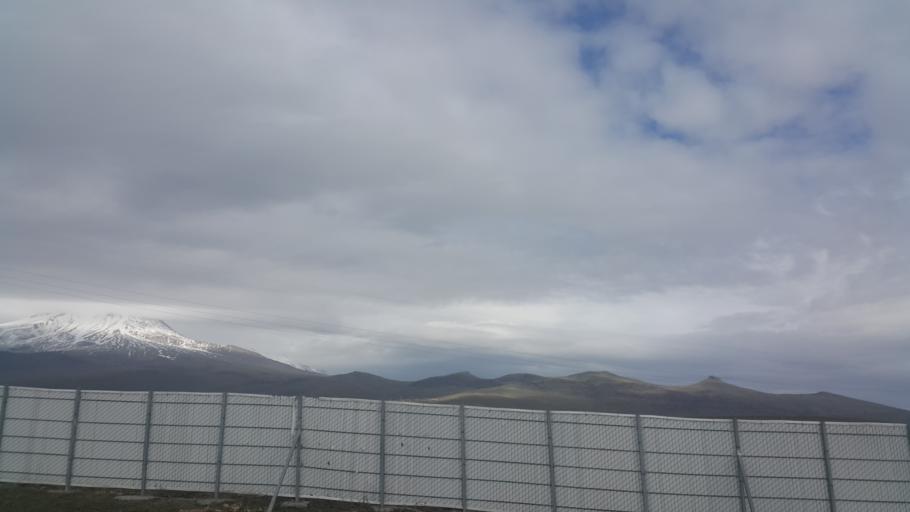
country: TR
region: Aksaray
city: Taspinar
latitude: 38.0819
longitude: 34.0329
